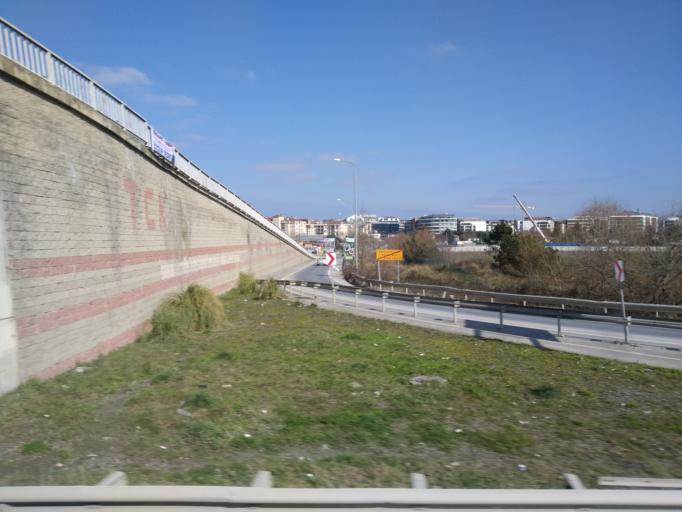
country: TR
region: Istanbul
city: Kemerburgaz
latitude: 41.1762
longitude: 28.8790
